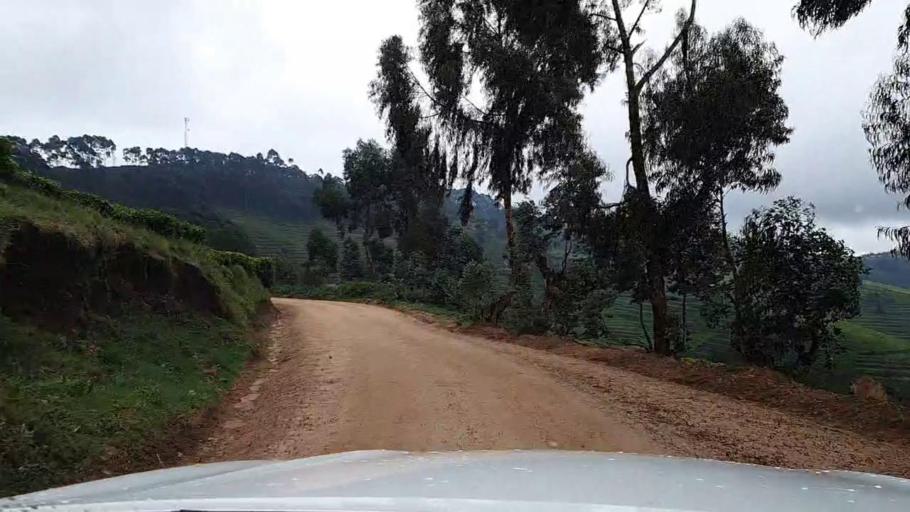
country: RW
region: Western Province
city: Kibuye
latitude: -2.2945
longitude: 29.3831
